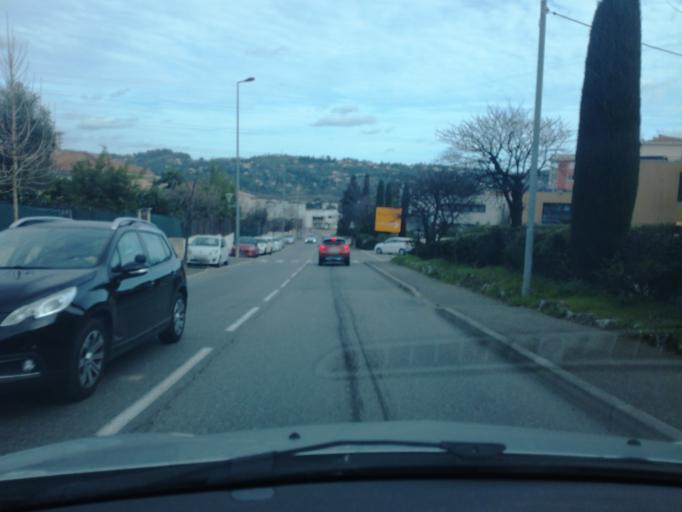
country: FR
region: Provence-Alpes-Cote d'Azur
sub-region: Departement des Alpes-Maritimes
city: Grasse
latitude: 43.6455
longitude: 6.9415
